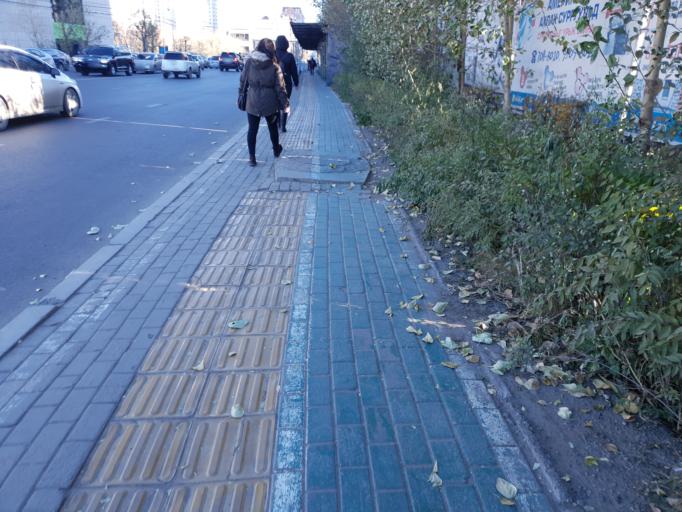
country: MN
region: Ulaanbaatar
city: Ulaanbaatar
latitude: 47.9001
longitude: 106.9097
